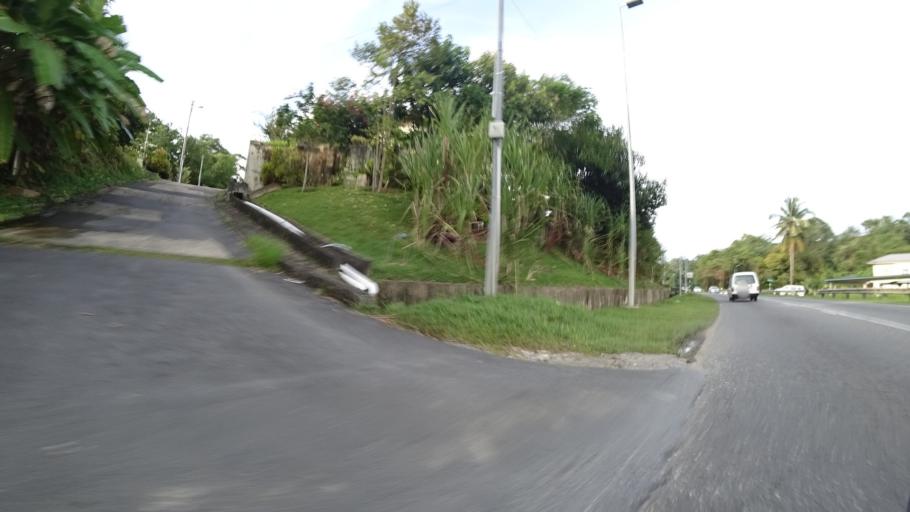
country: BN
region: Brunei and Muara
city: Bandar Seri Begawan
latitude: 4.8762
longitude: 114.8288
